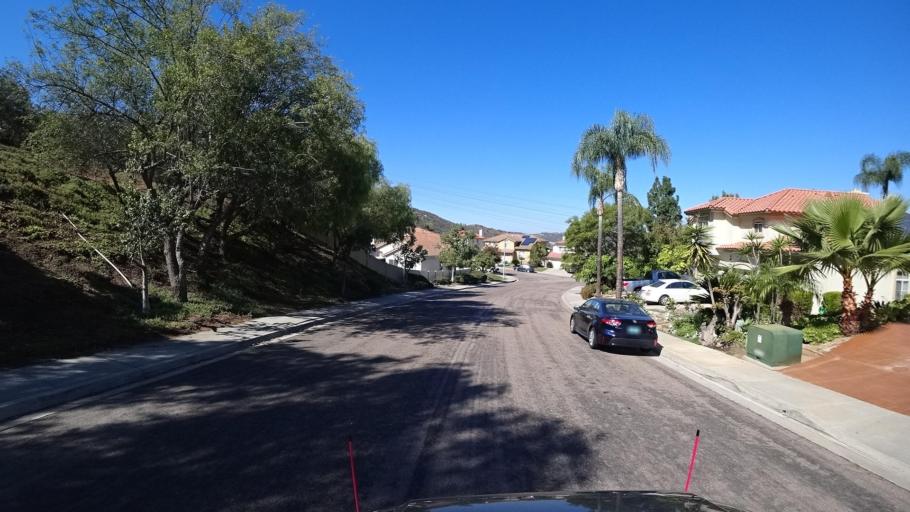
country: US
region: California
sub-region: San Diego County
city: Rancho San Diego
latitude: 32.7347
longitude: -116.9160
